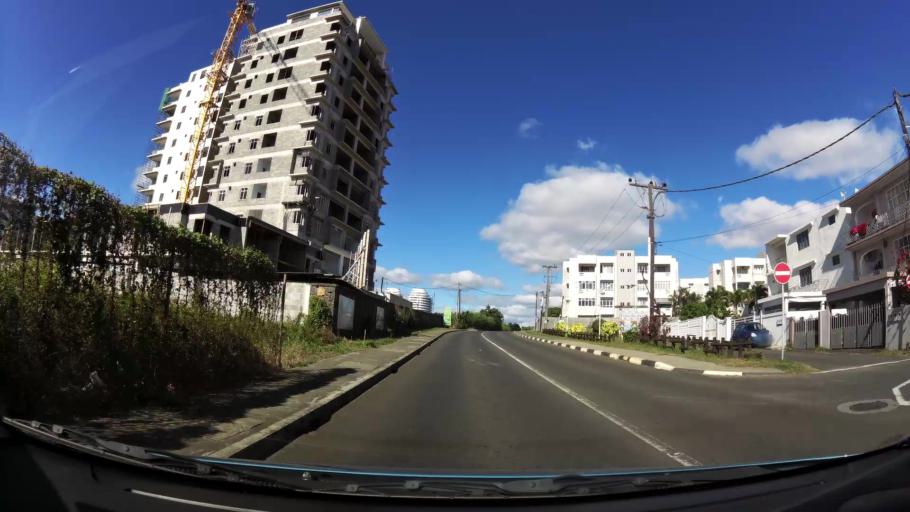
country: MU
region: Plaines Wilhems
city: Quatre Bornes
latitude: -20.2607
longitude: 57.4871
